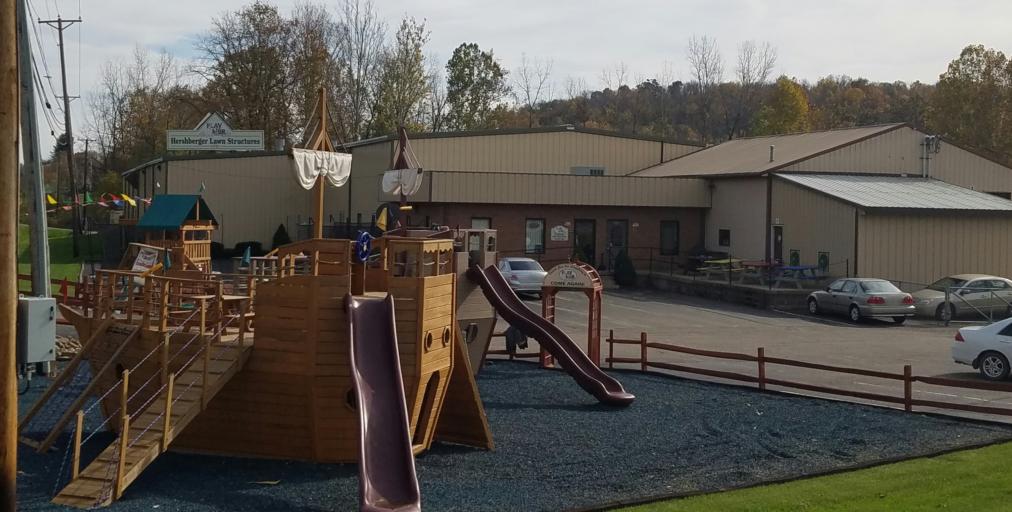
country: US
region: Ohio
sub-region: Holmes County
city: Millersburg
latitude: 40.5615
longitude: -81.9478
